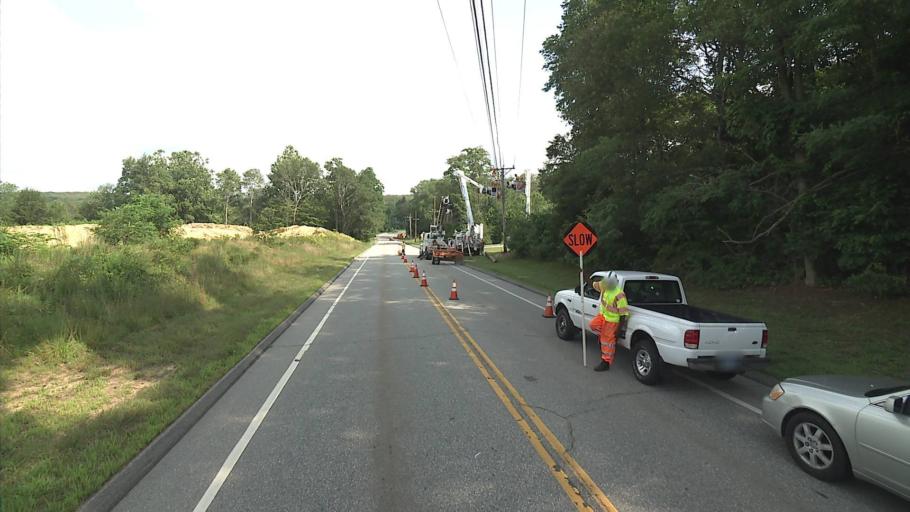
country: US
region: Connecticut
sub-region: New London County
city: Colchester
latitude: 41.5776
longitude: -72.4018
